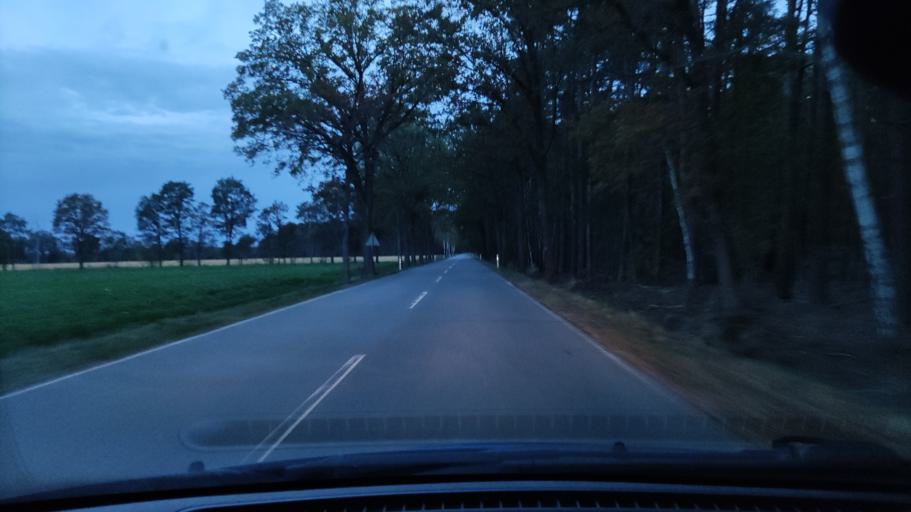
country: DE
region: Lower Saxony
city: Trebel
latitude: 52.9594
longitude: 11.3161
